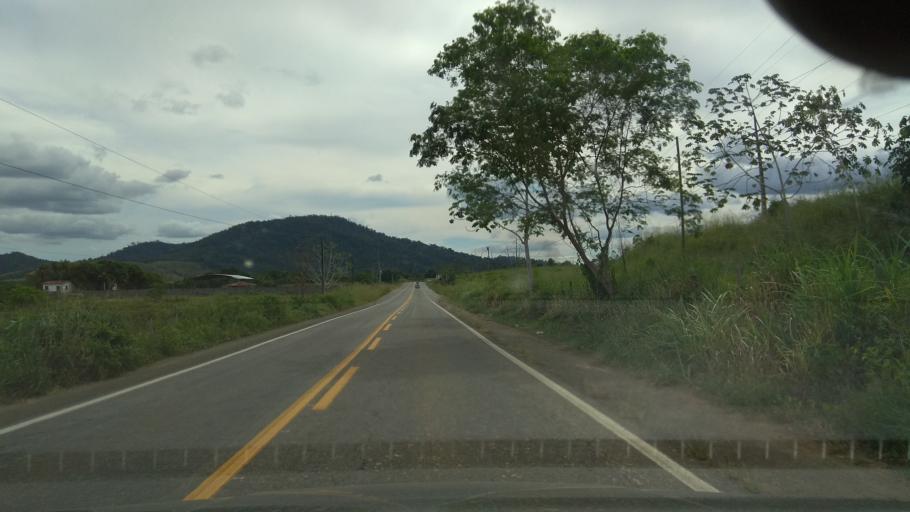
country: BR
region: Bahia
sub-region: Ipiau
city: Ipiau
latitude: -14.1764
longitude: -39.6742
